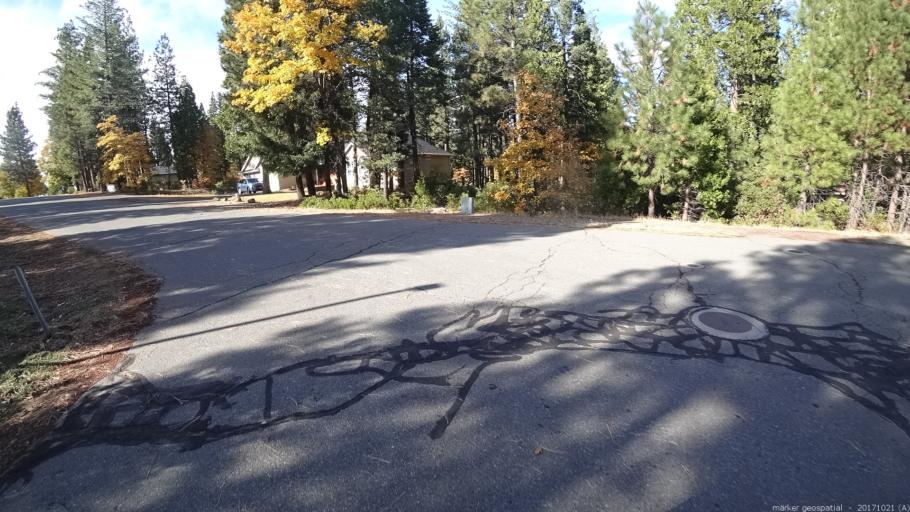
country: US
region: California
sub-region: Shasta County
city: Burney
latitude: 40.8743
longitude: -121.6589
